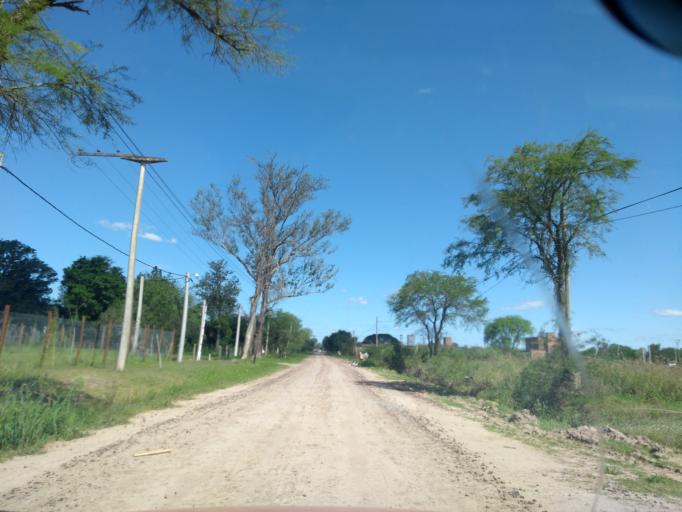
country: AR
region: Chaco
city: Resistencia
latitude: -27.4236
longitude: -58.9458
